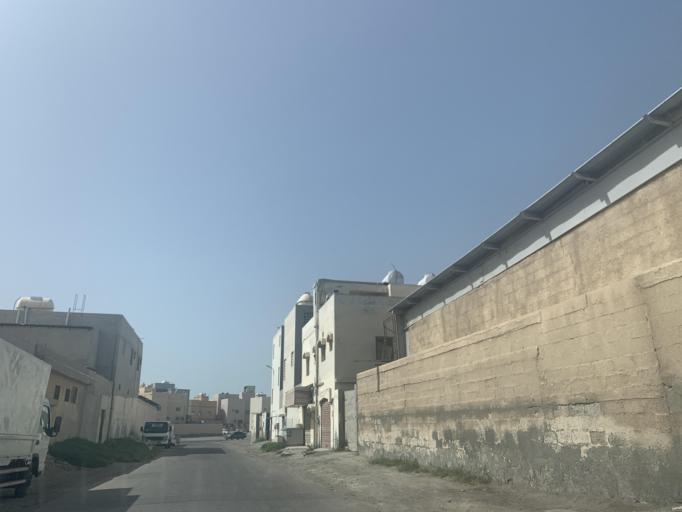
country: BH
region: Northern
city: Sitrah
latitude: 26.1677
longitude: 50.6158
